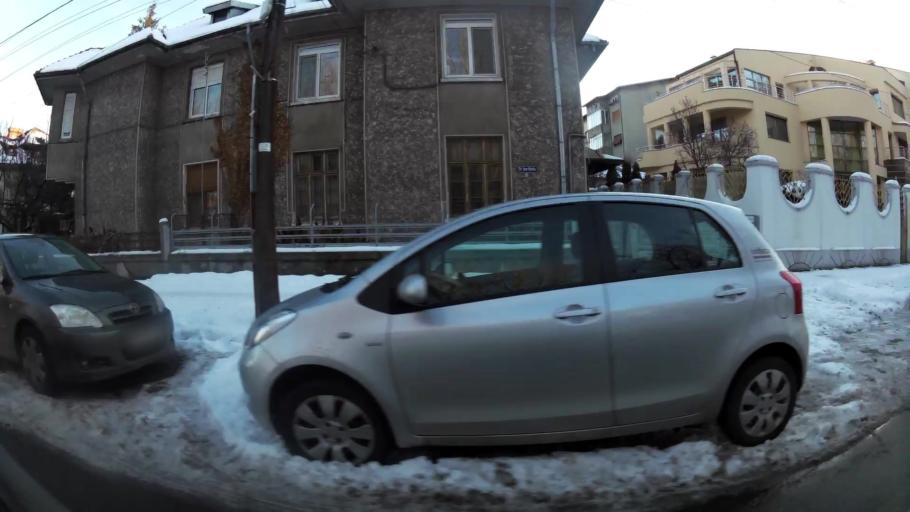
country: RO
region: Bucuresti
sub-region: Municipiul Bucuresti
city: Bucuresti
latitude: 44.4328
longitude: 26.0659
